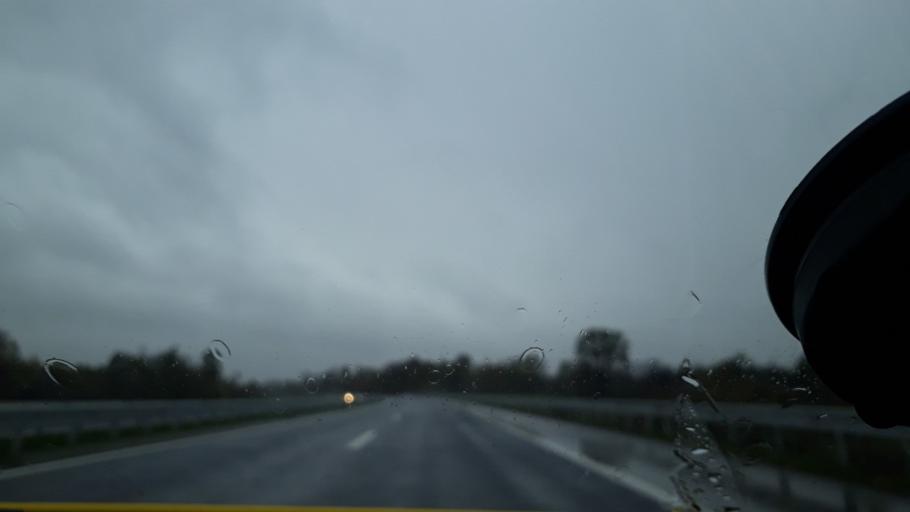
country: BA
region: Republika Srpska
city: Maglajani
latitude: 44.8909
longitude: 17.3697
